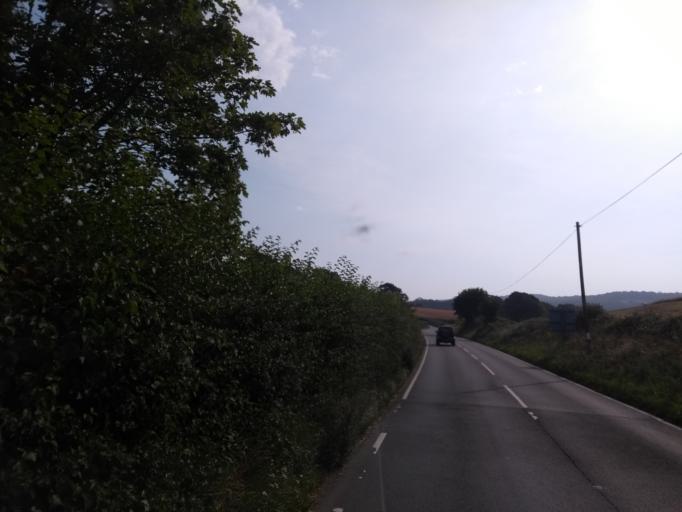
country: GB
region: England
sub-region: Devon
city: Axminster
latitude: 50.7587
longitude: -3.0231
